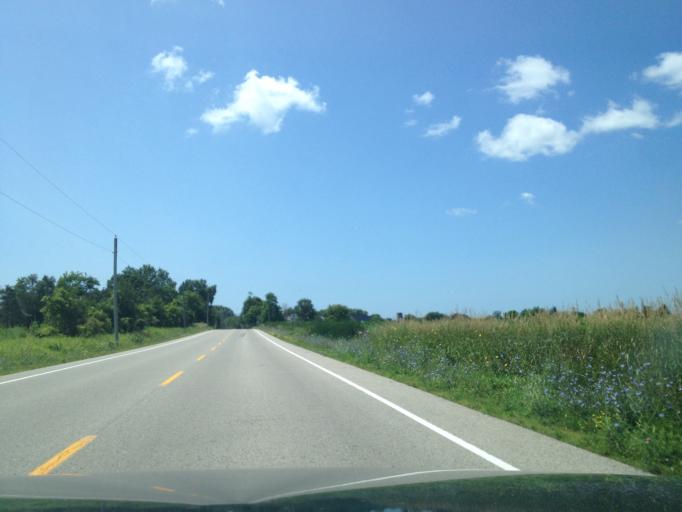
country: CA
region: Ontario
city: Norfolk County
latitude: 42.6014
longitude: -80.4798
